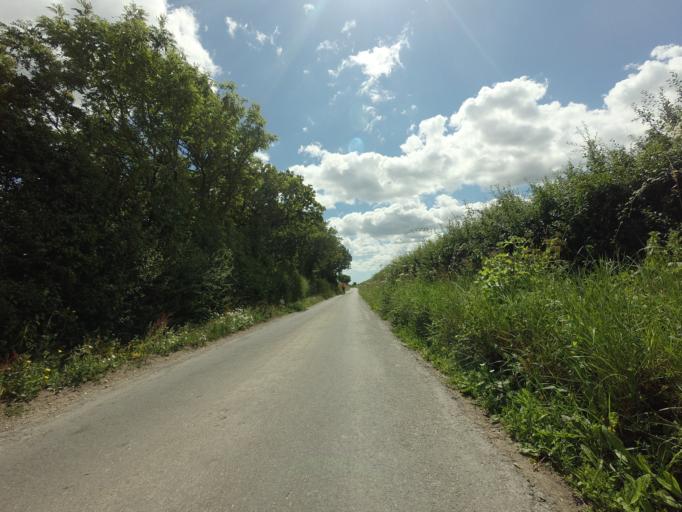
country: GB
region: England
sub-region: East Sussex
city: Seaford
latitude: 50.8580
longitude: 0.1515
